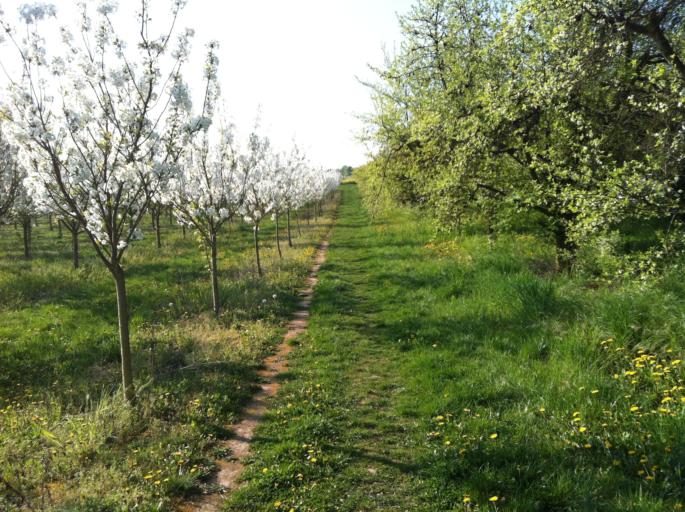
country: DE
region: Rheinland-Pfalz
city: Budenheim
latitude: 49.9893
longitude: 8.1899
